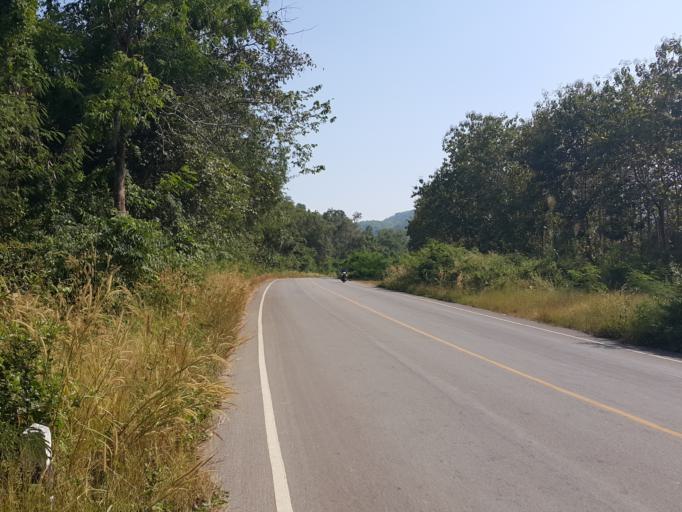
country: TH
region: Sukhothai
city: Thung Saliam
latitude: 17.3391
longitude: 99.4743
